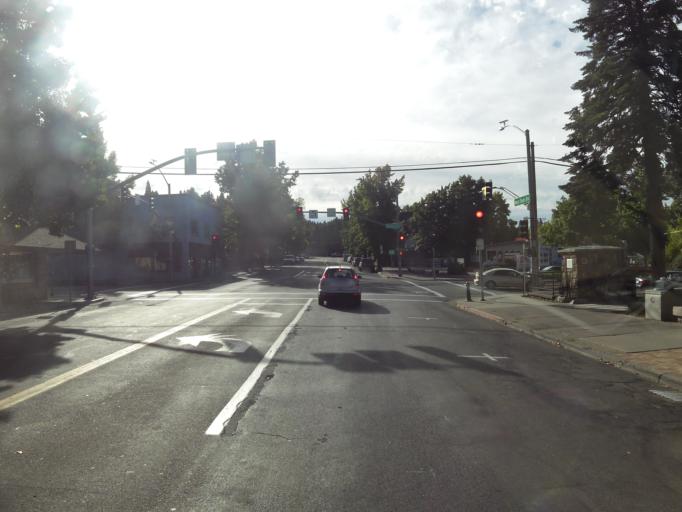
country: US
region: California
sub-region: Siskiyou County
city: Mount Shasta
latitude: 41.3135
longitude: -122.3126
